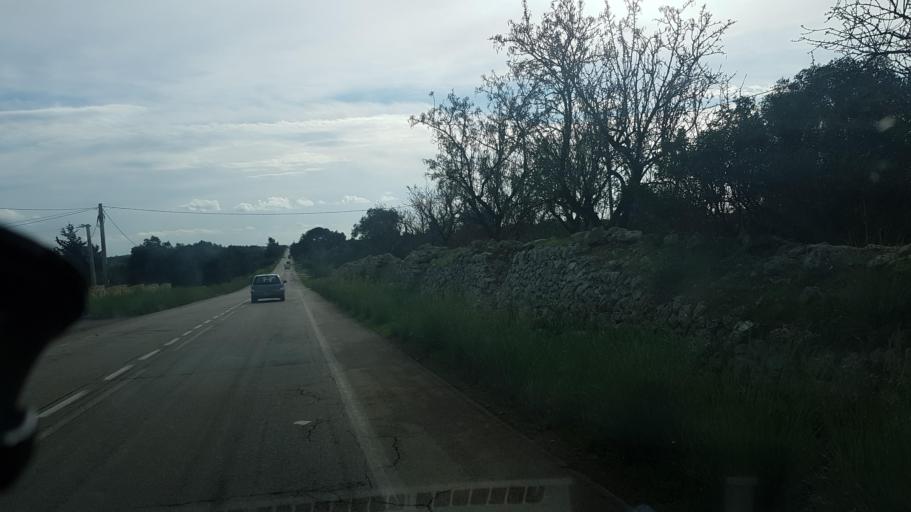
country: IT
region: Apulia
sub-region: Provincia di Brindisi
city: Carovigno
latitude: 40.6864
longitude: 17.6781
